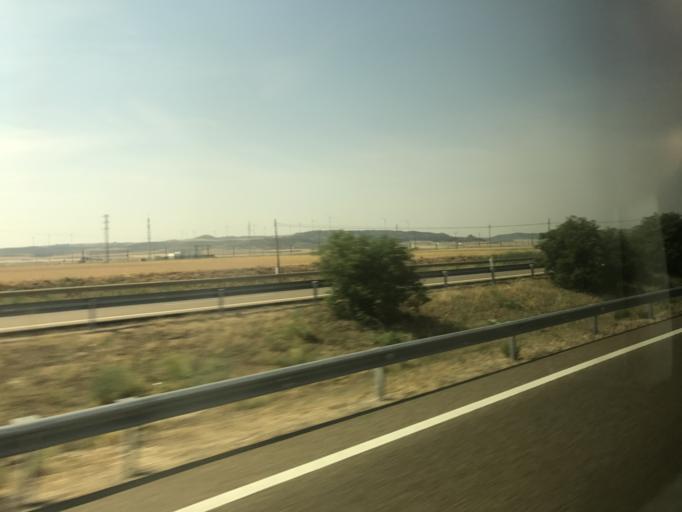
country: ES
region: Castille and Leon
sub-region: Provincia de Palencia
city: Quintana del Puente
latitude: 42.0669
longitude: -4.2252
